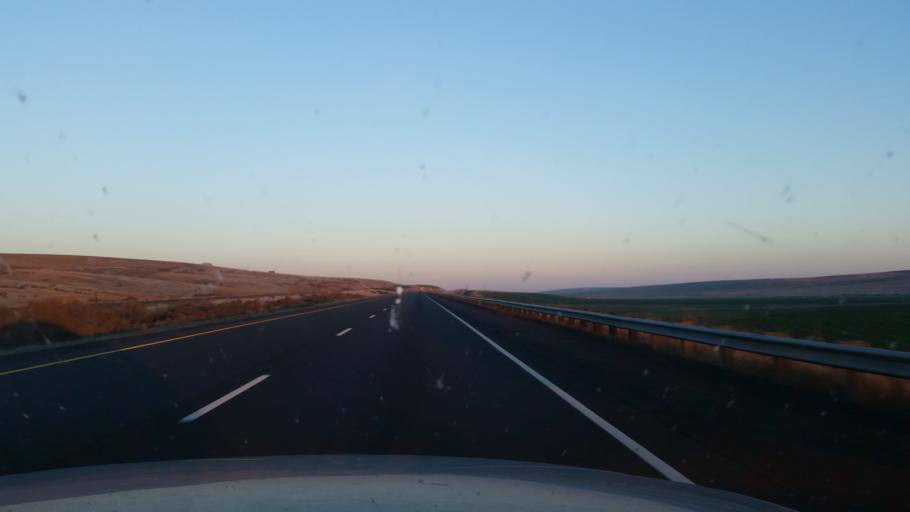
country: US
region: Washington
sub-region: Grant County
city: Warden
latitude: 47.0844
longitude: -118.9748
